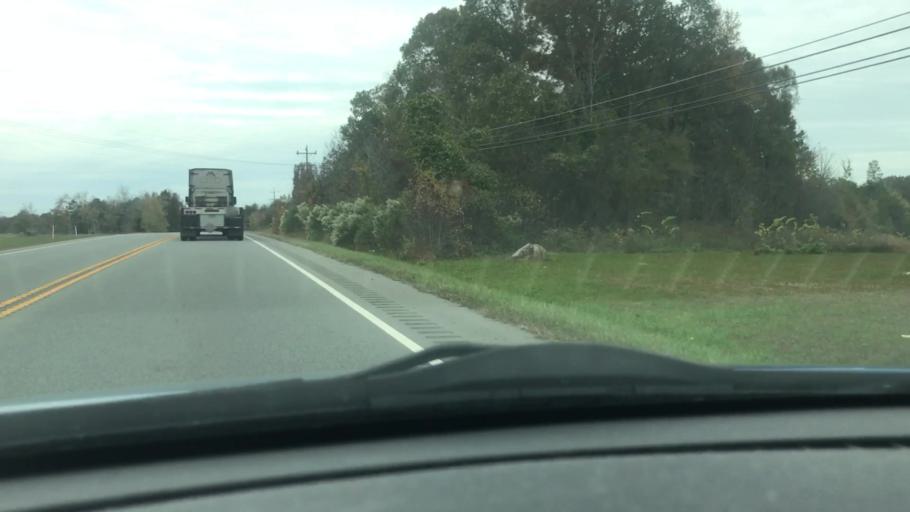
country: US
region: North Carolina
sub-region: Davidson County
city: Thomasville
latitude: 35.7749
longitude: -80.1117
